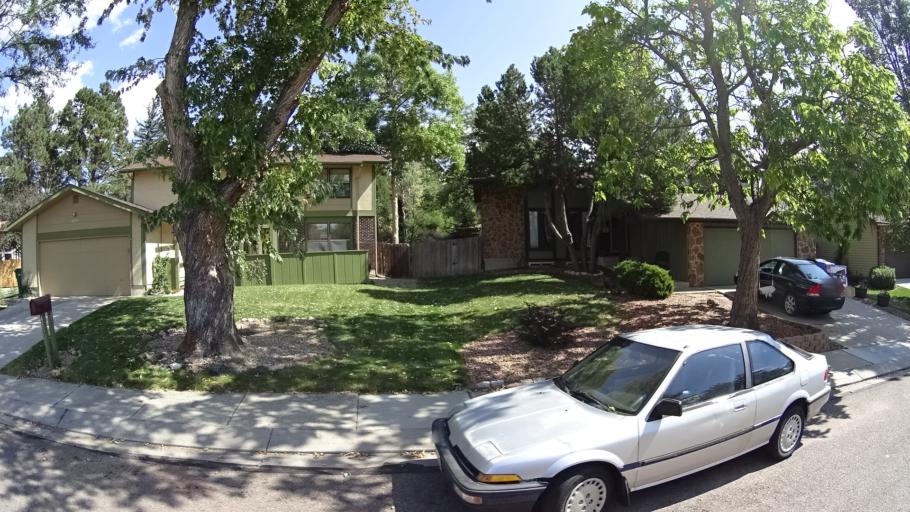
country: US
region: Colorado
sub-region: El Paso County
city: Cimarron Hills
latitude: 38.8737
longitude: -104.7440
